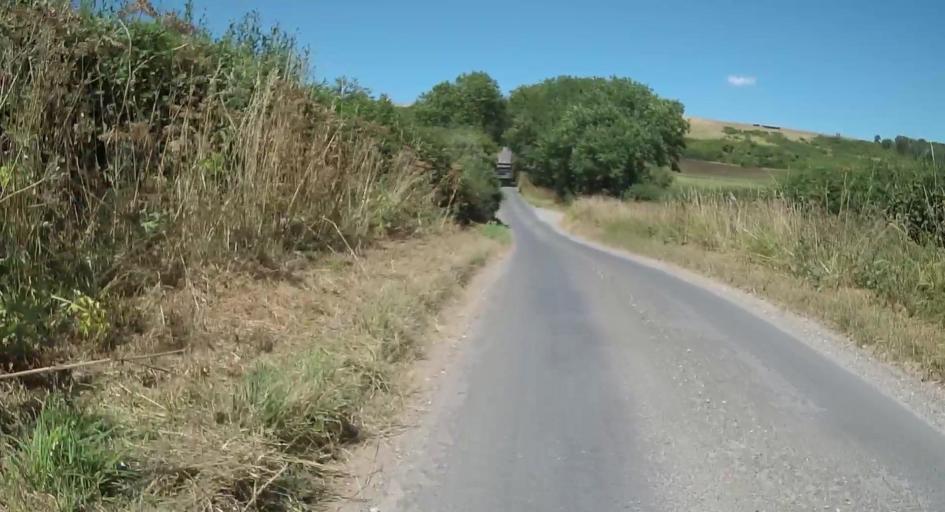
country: GB
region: England
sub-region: Dorset
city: Bovington Camp
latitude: 50.6541
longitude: -2.2982
